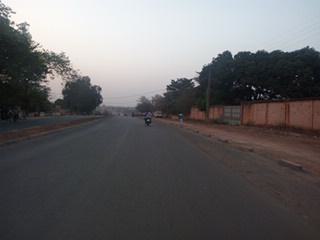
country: BJ
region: Borgou
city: Parakou
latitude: 9.3417
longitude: 2.6053
